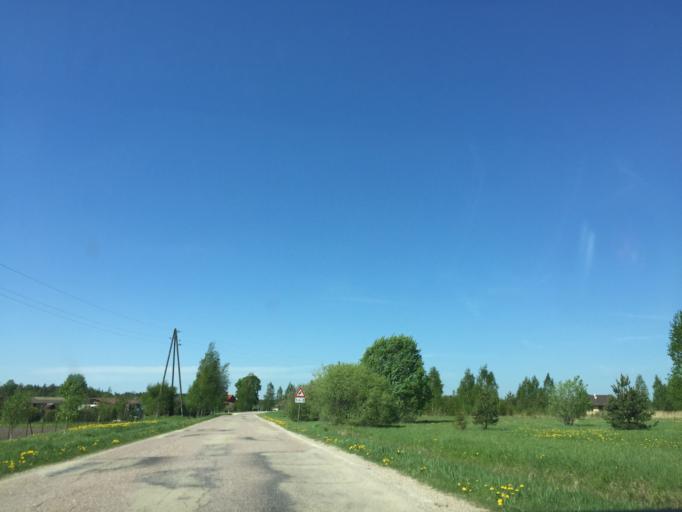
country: LV
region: Ogre
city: Ogre
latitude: 56.8525
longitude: 24.7121
